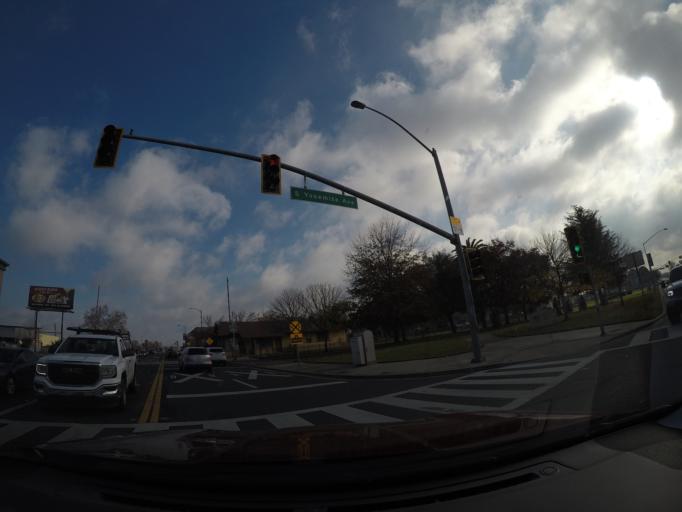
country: US
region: California
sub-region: Stanislaus County
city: Oakdale
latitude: 37.7667
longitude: -120.8469
